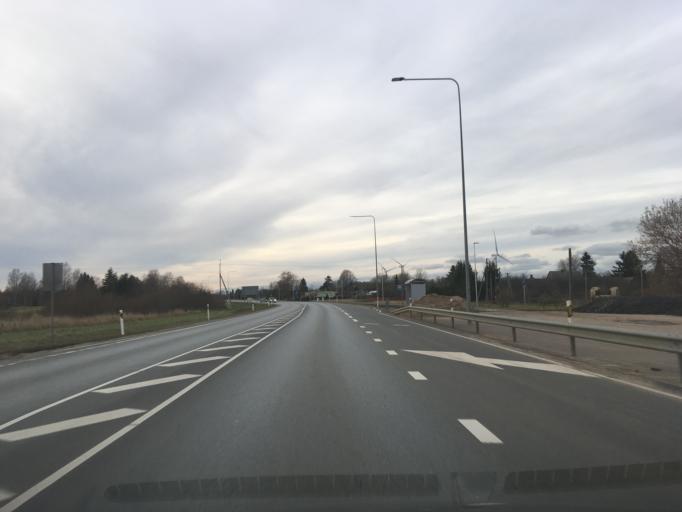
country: EE
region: Ida-Virumaa
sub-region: Aseri vald
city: Aseri
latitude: 59.4398
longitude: 26.8469
